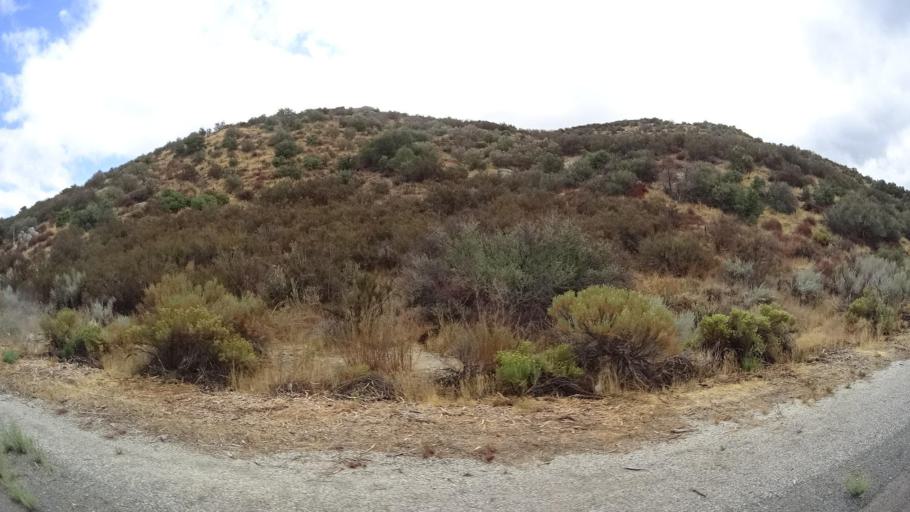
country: US
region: California
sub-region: San Diego County
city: Campo
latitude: 32.7045
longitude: -116.4318
